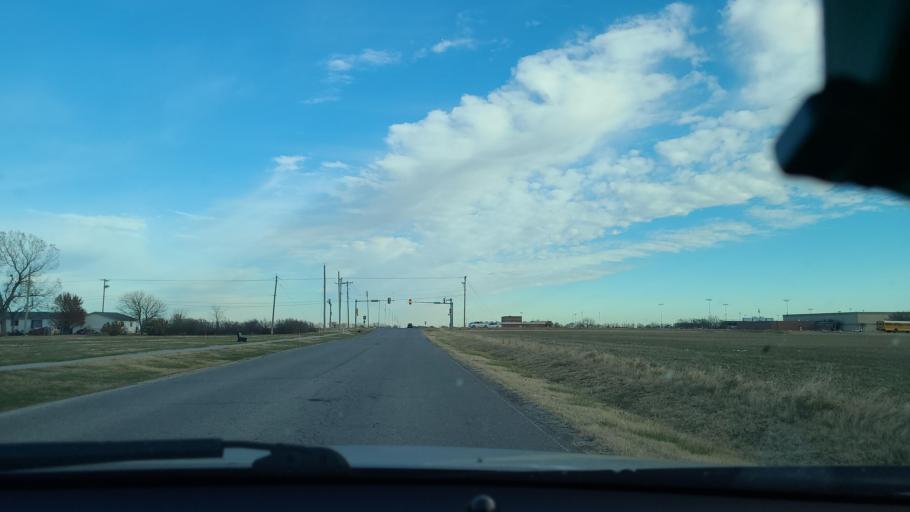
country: US
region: Kansas
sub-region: Sedgwick County
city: Goddard
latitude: 37.6499
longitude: -97.5732
